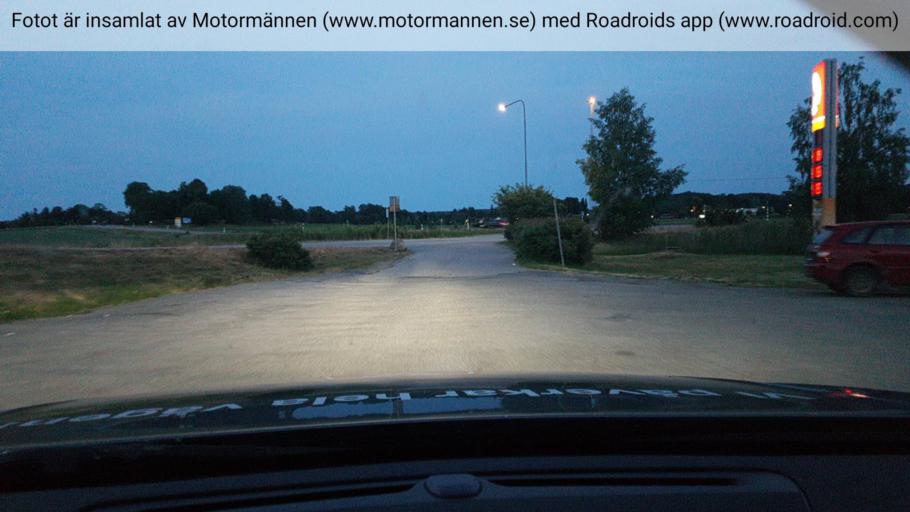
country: SE
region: Stockholm
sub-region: Sodertalje Kommun
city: Pershagen
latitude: 59.0870
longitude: 17.6033
